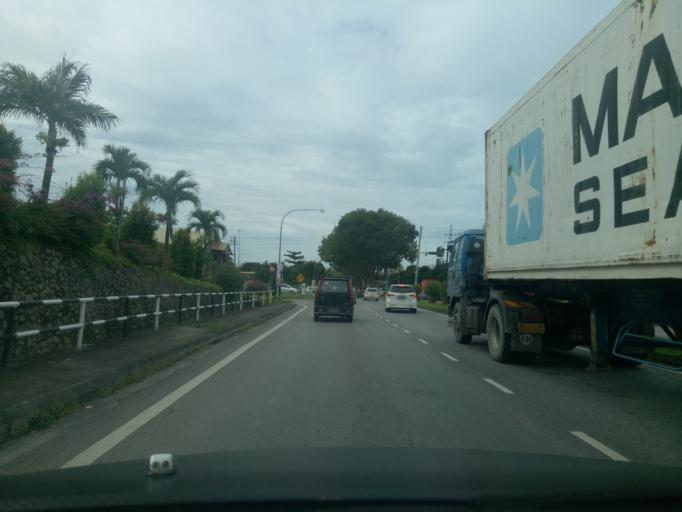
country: MY
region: Sarawak
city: Kuching
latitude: 1.5376
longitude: 110.3683
